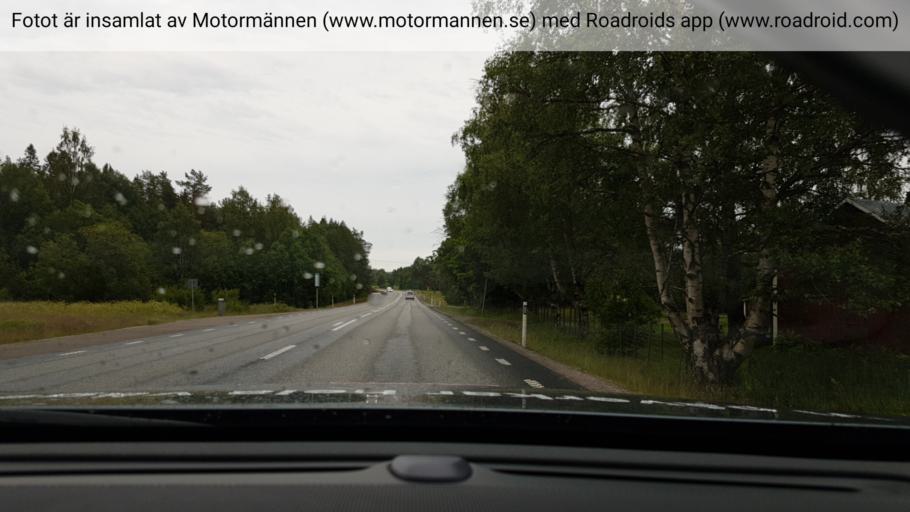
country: SE
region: Vaesterbotten
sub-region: Umea Kommun
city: Roback
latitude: 63.8587
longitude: 20.0922
